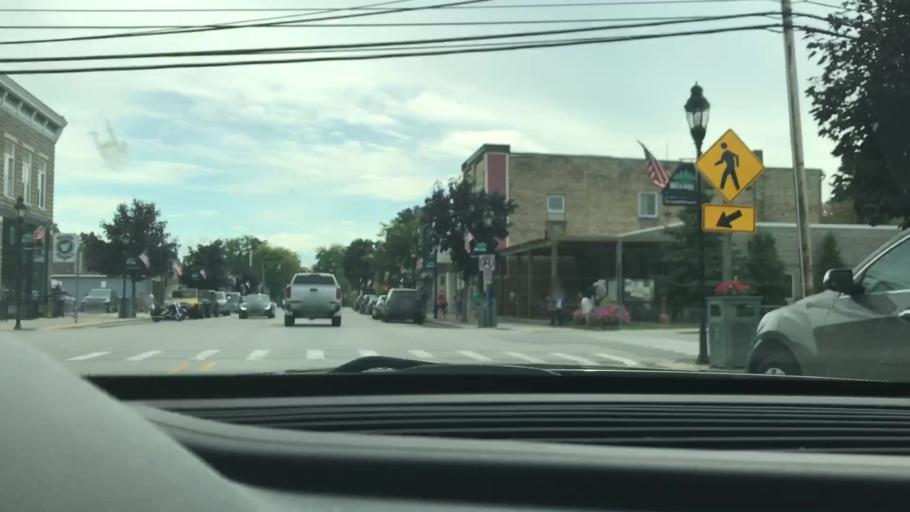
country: US
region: Michigan
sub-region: Antrim County
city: Bellaire
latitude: 44.9767
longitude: -85.2099
